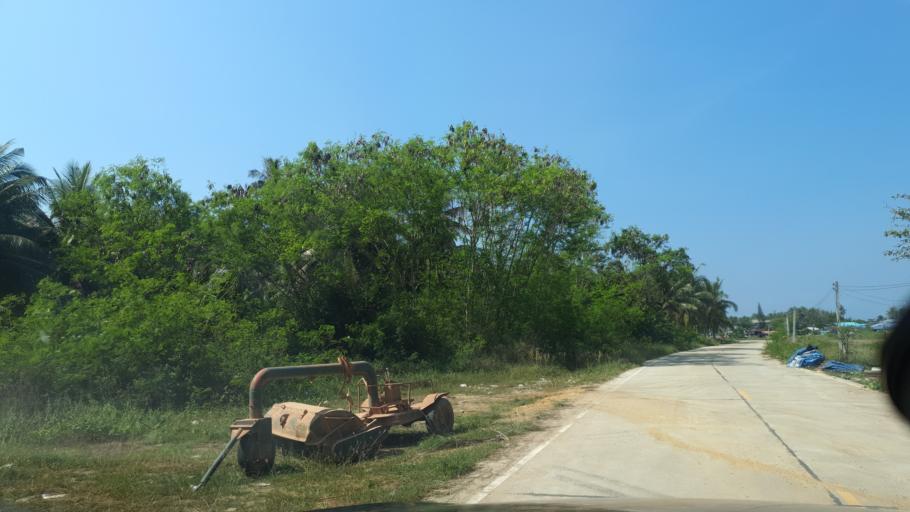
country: TH
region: Surat Thani
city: Tha Chana
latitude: 9.5999
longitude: 99.2090
